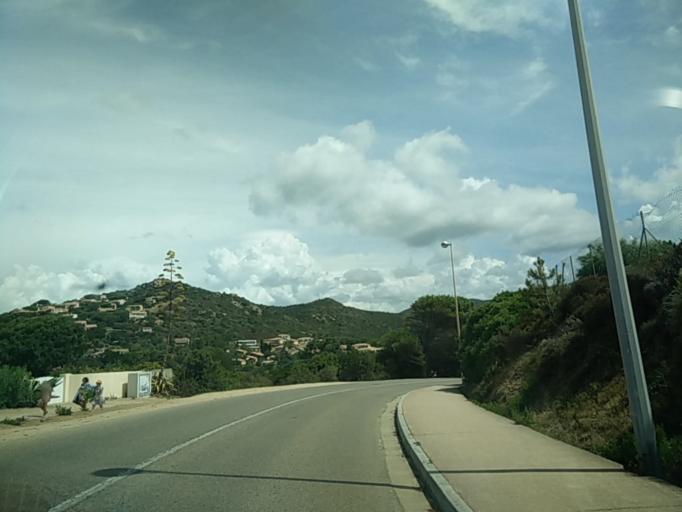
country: FR
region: Corsica
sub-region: Departement de la Corse-du-Sud
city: Pietrosella
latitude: 41.8292
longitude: 8.7845
